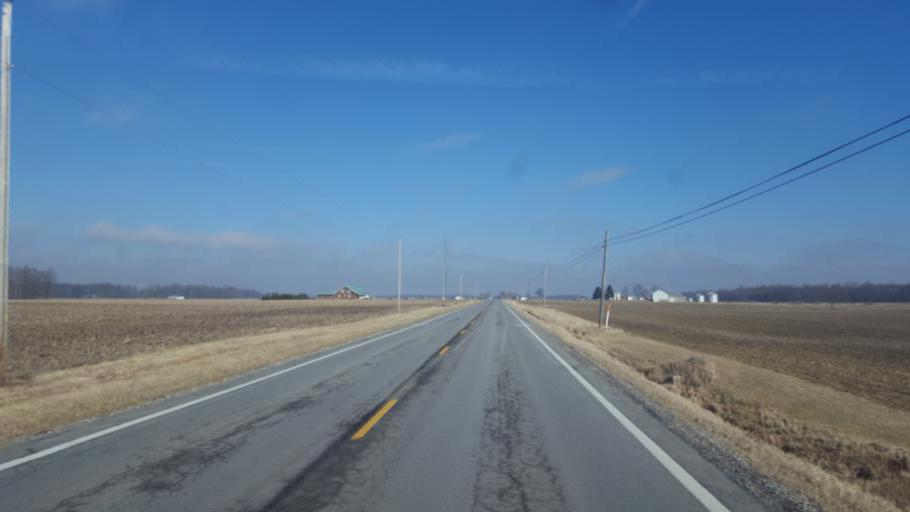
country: US
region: Ohio
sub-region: Crawford County
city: Bucyrus
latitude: 40.9243
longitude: -82.9510
